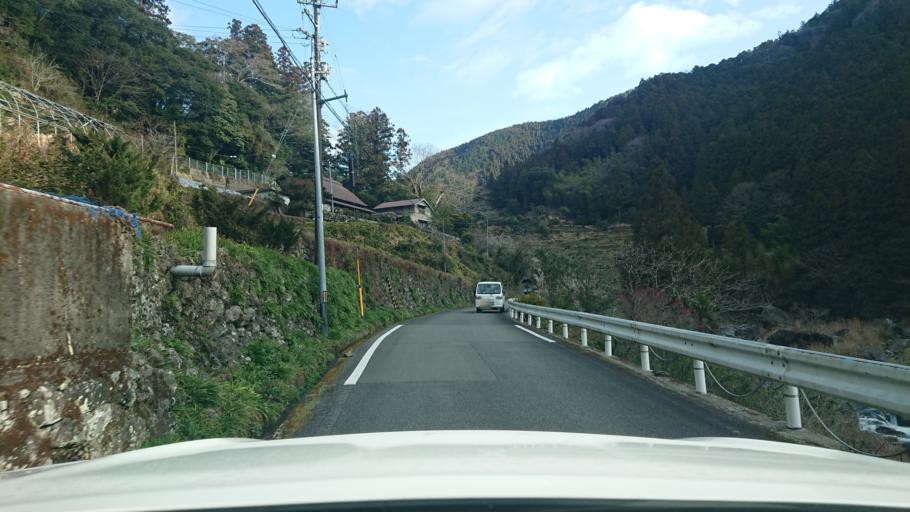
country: JP
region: Tokushima
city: Kamojimacho-jogejima
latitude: 33.9010
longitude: 134.3949
